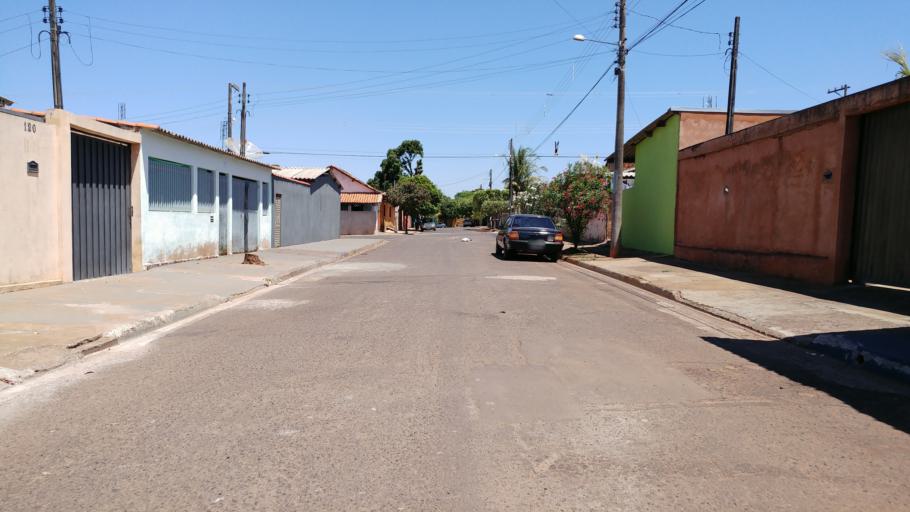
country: BR
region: Sao Paulo
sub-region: Paraguacu Paulista
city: Paraguacu Paulista
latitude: -22.4088
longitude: -50.5689
